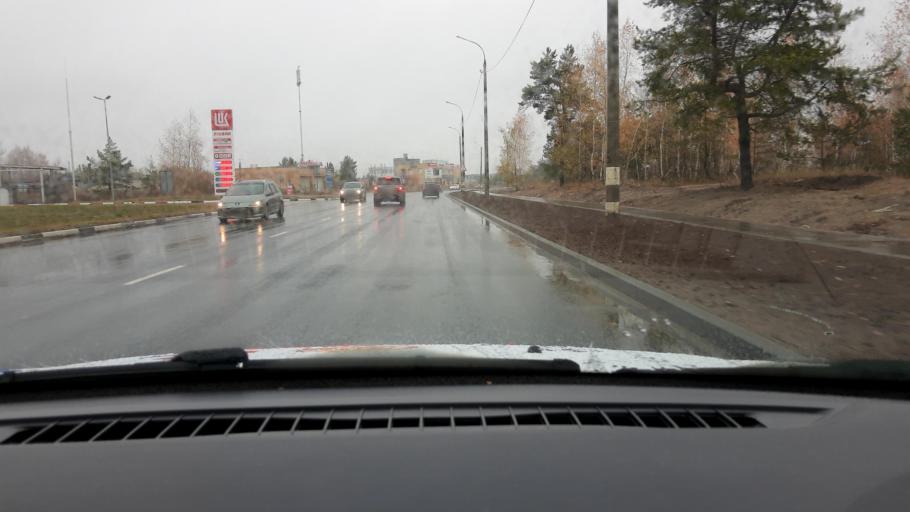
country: RU
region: Nizjnij Novgorod
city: Dzerzhinsk
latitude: 56.2369
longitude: 43.4077
